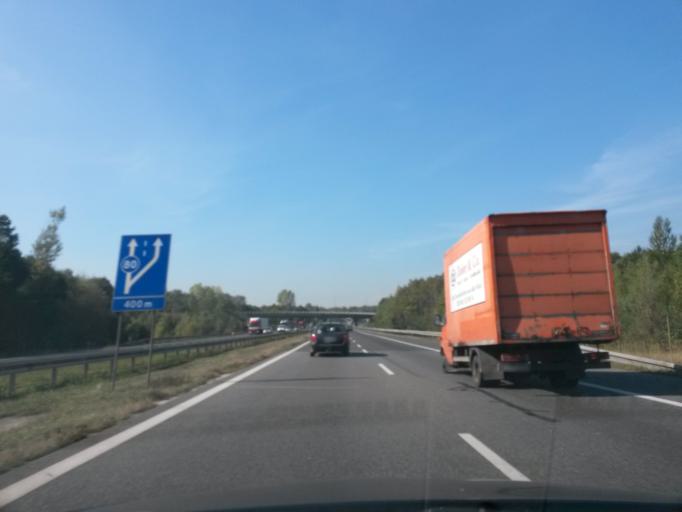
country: PL
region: Silesian Voivodeship
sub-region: Katowice
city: Murcki
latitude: 50.2292
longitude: 19.0726
